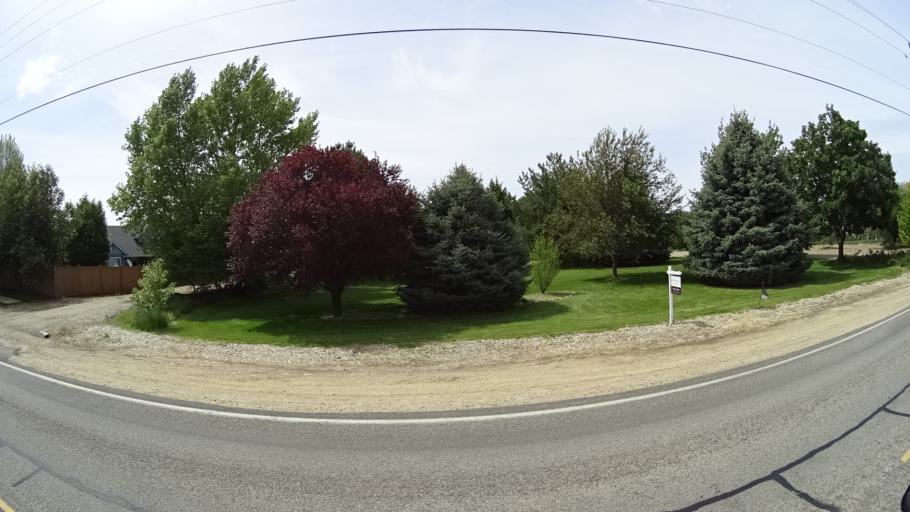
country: US
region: Idaho
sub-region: Ada County
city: Meridian
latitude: 43.5612
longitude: -116.3295
